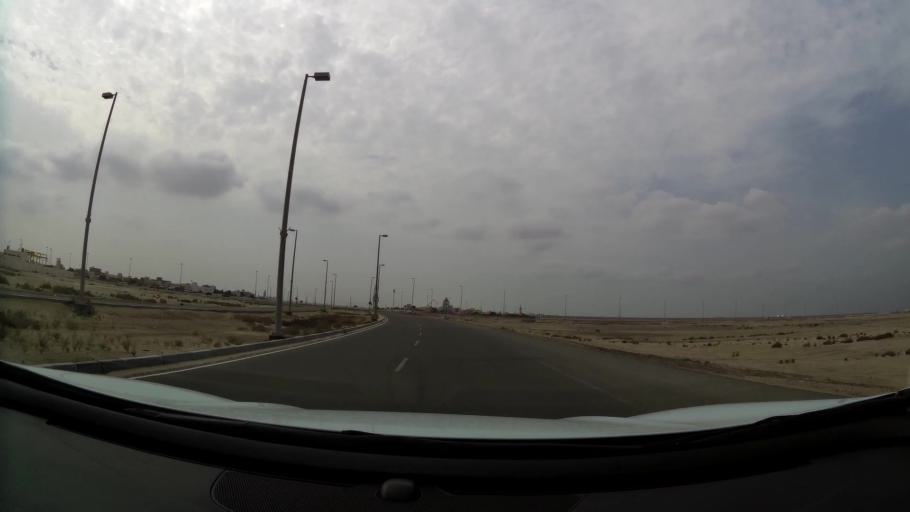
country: AE
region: Abu Dhabi
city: Abu Dhabi
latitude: 24.6413
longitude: 54.6643
